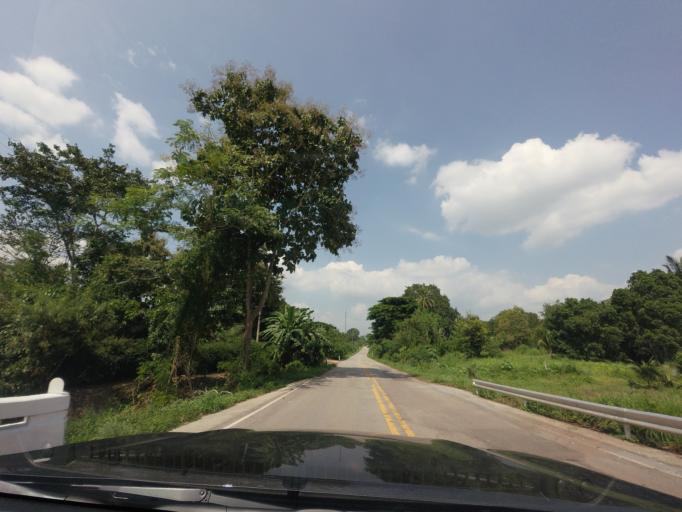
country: TH
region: Uttaradit
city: Ban Khok
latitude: 18.0000
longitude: 101.0332
